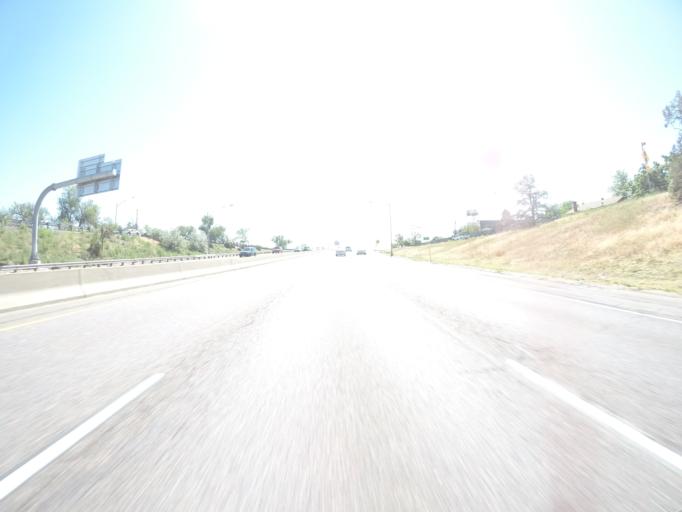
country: US
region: Colorado
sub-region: Adams County
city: Berkley
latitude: 39.7842
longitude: -105.0248
